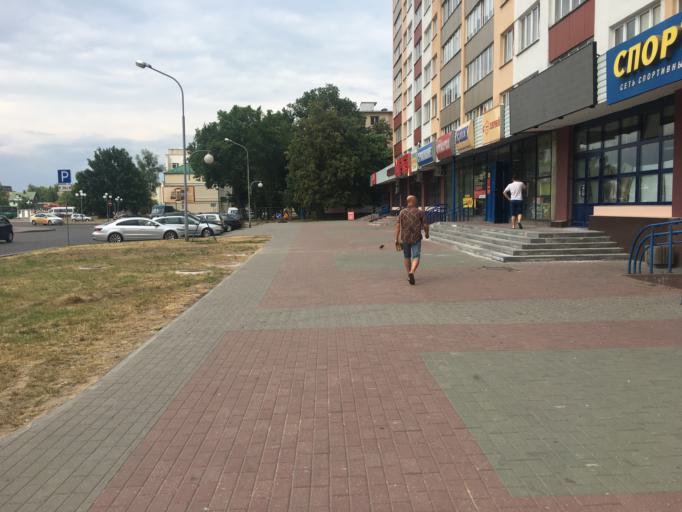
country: BY
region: Grodnenskaya
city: Hrodna
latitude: 53.6765
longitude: 23.8448
